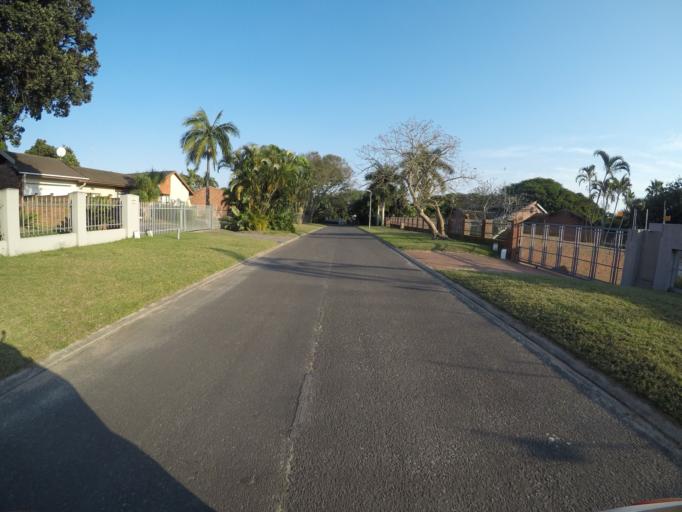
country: ZA
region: KwaZulu-Natal
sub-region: uThungulu District Municipality
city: Richards Bay
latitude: -28.7717
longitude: 32.1158
